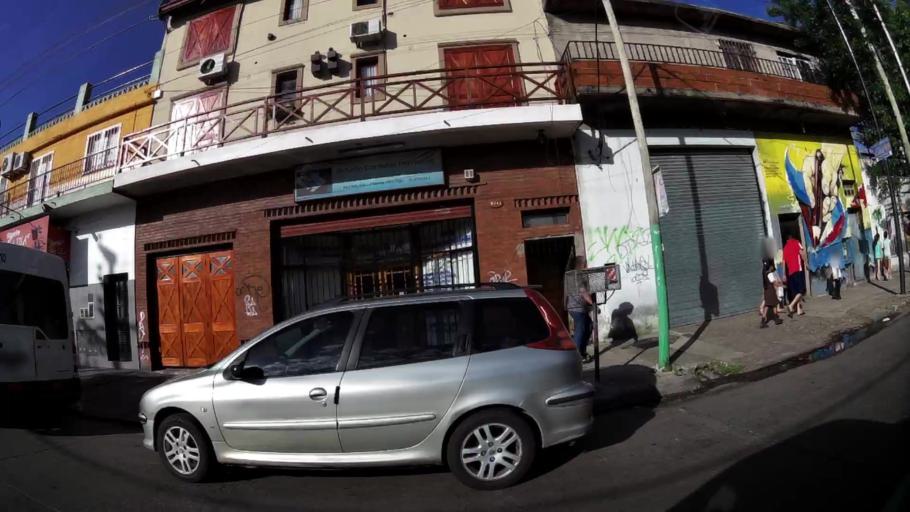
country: AR
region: Buenos Aires
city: Hurlingham
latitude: -34.5735
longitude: -58.6119
